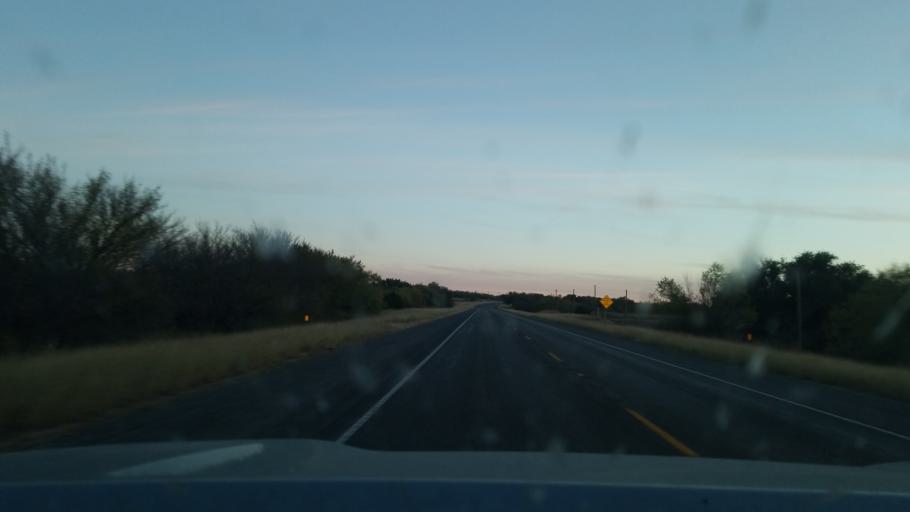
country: US
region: Texas
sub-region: Stephens County
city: Breckenridge
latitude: 32.5816
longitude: -98.8964
